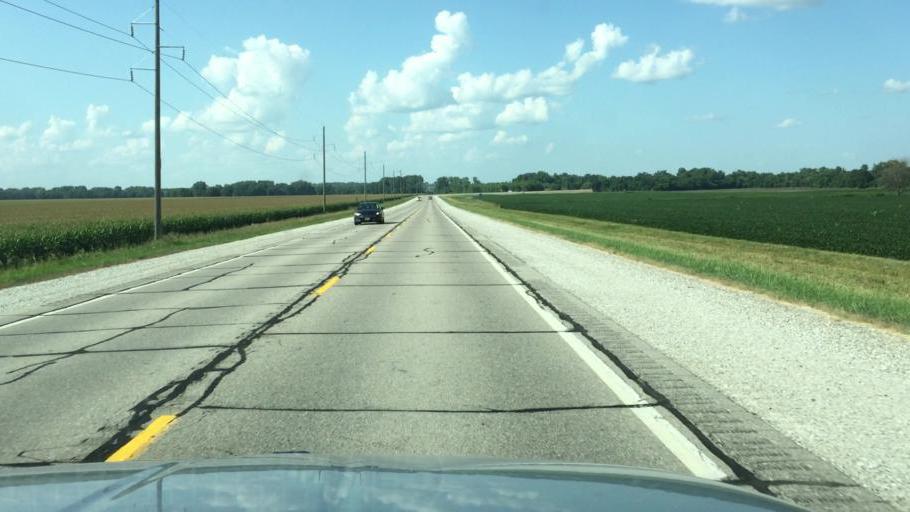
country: US
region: Iowa
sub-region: Jasper County
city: Monroe
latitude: 41.6100
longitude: -93.0962
